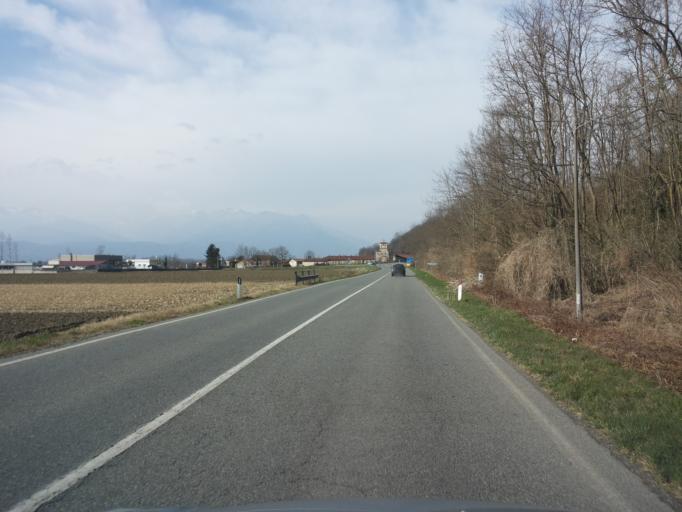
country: IT
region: Piedmont
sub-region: Provincia di Torino
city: Vestigne
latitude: 45.3949
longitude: 7.9446
